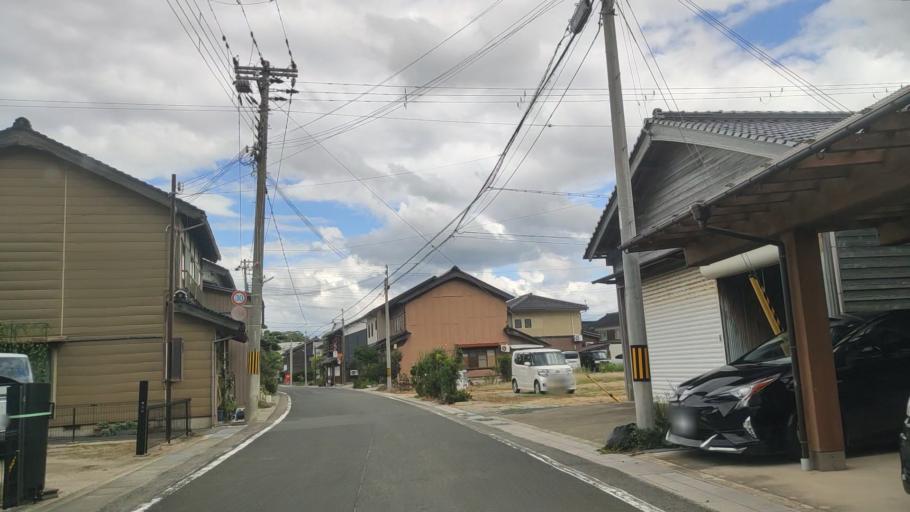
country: JP
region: Hyogo
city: Toyooka
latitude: 35.6430
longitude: 134.9030
